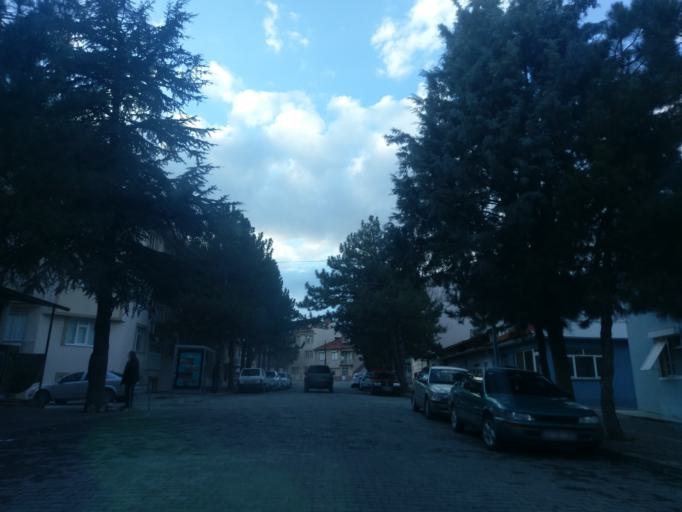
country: TR
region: Kuetahya
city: Gediz
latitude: 38.9909
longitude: 29.3884
